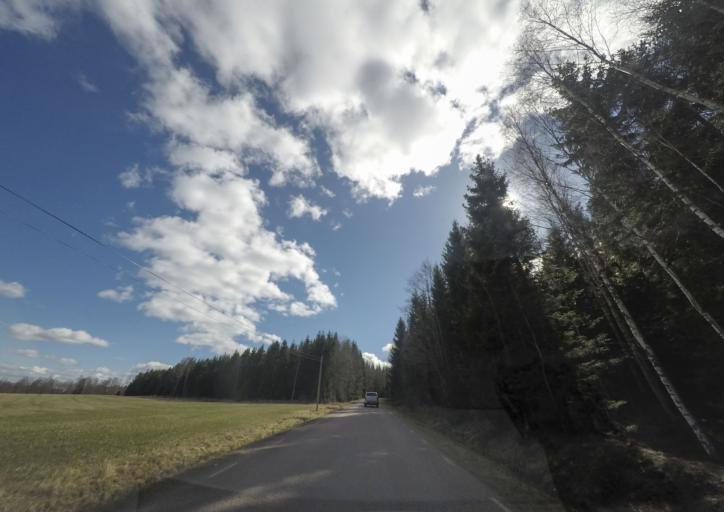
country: SE
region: OEstergoetland
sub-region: Norrkopings Kommun
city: Krokek
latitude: 58.7387
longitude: 16.4714
